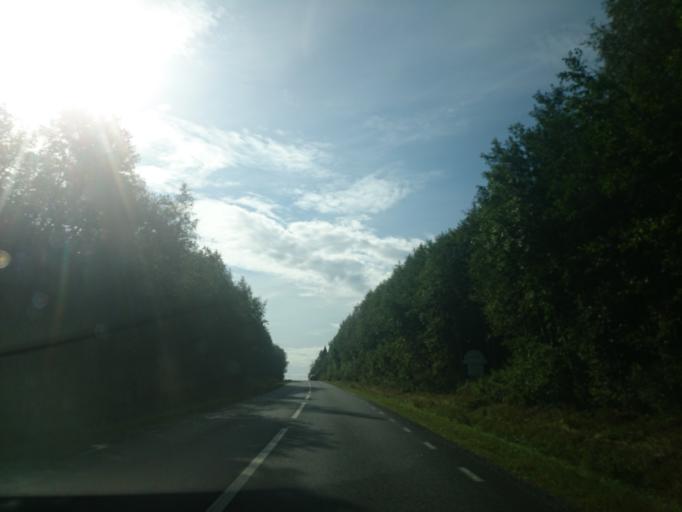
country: SE
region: Vaesternorrland
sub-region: Kramfors Kommun
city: Nordingra
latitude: 62.9403
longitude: 18.2587
